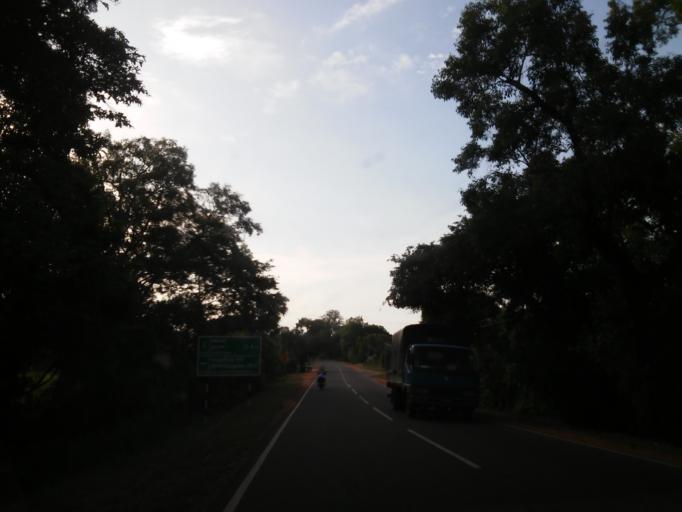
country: LK
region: Central
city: Sigiriya
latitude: 8.0901
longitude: 80.6364
